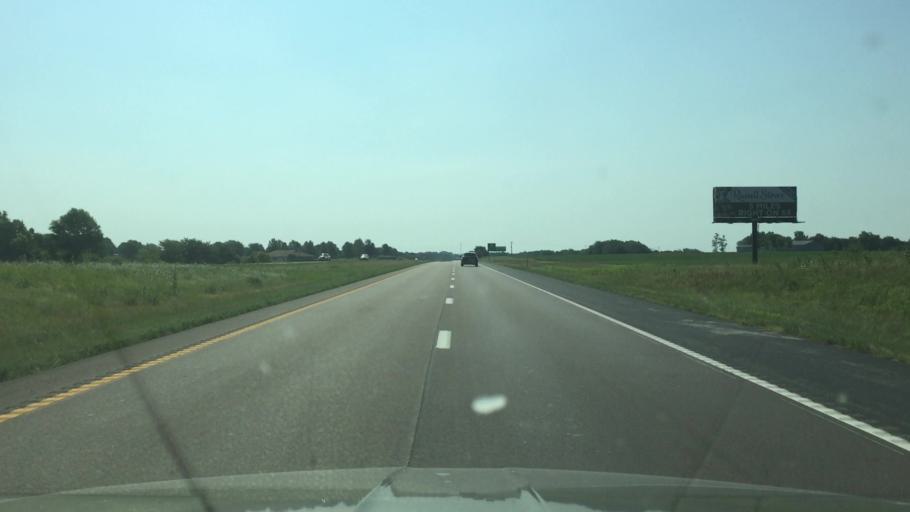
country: US
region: Missouri
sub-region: Pettis County
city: La Monte
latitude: 38.7503
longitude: -93.3480
